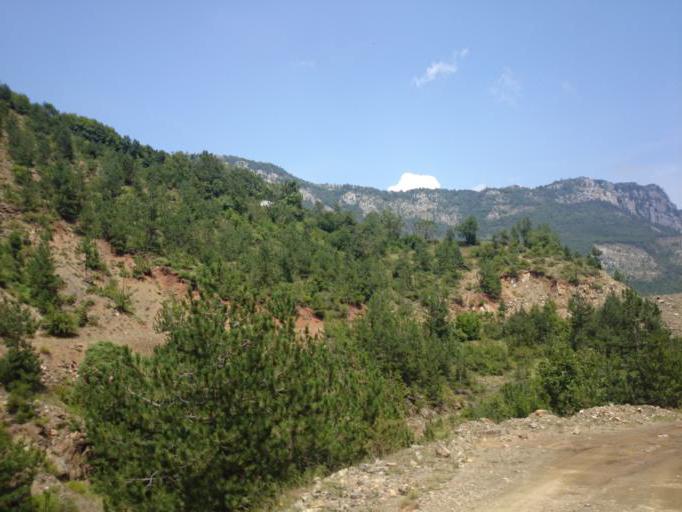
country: AL
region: Diber
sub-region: Rrethi i Dibres
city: Fushe-Lure
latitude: 41.8304
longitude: 20.1797
